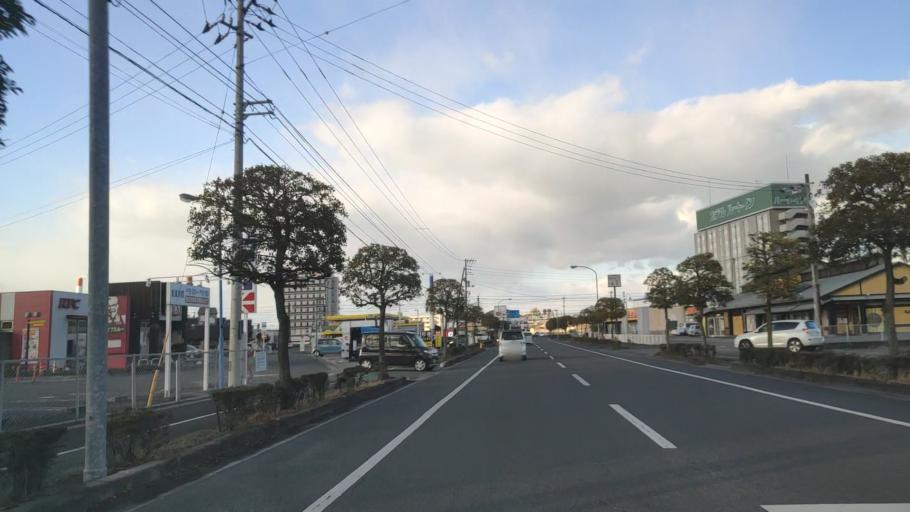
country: JP
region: Ehime
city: Saijo
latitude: 33.9261
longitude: 133.1836
